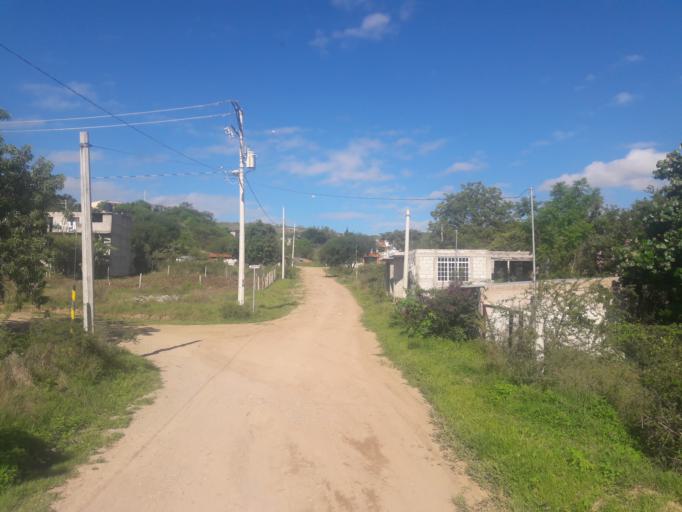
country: MX
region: Oaxaca
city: Ciudad de Huajuapam de Leon
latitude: 17.8368
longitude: -97.7872
